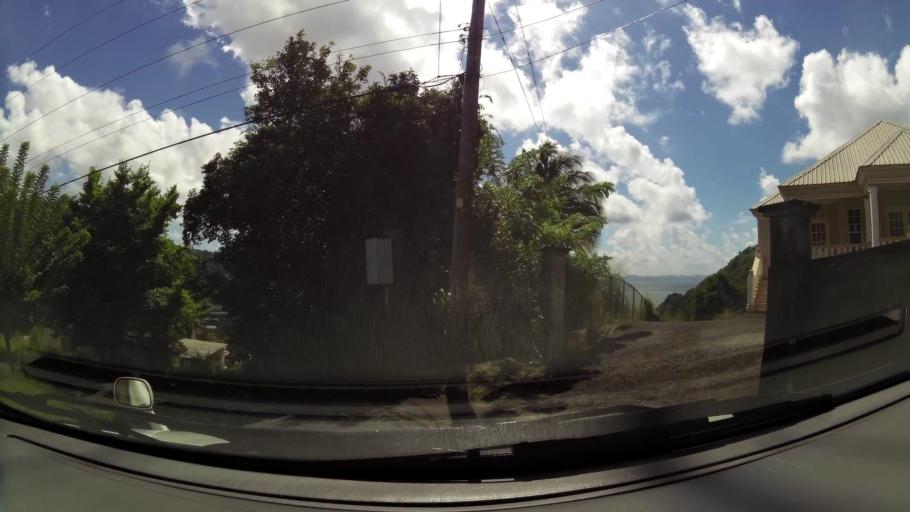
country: VC
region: Saint George
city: Kingstown Park
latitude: 13.1615
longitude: -61.2321
